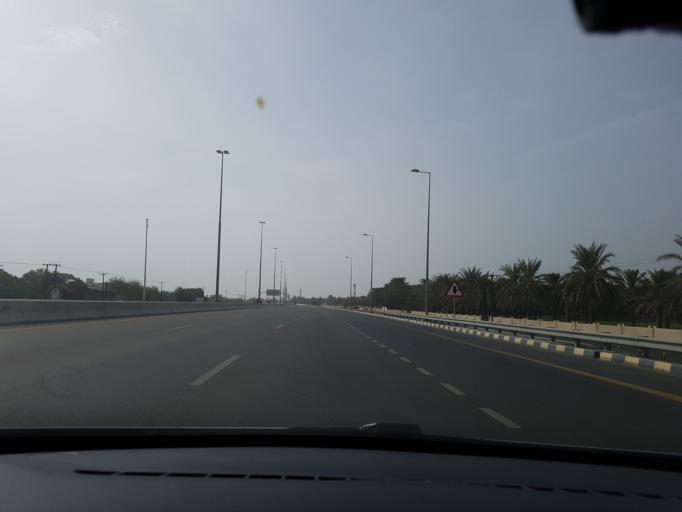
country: OM
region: Al Batinah
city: Al Sohar
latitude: 24.3323
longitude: 56.7392
